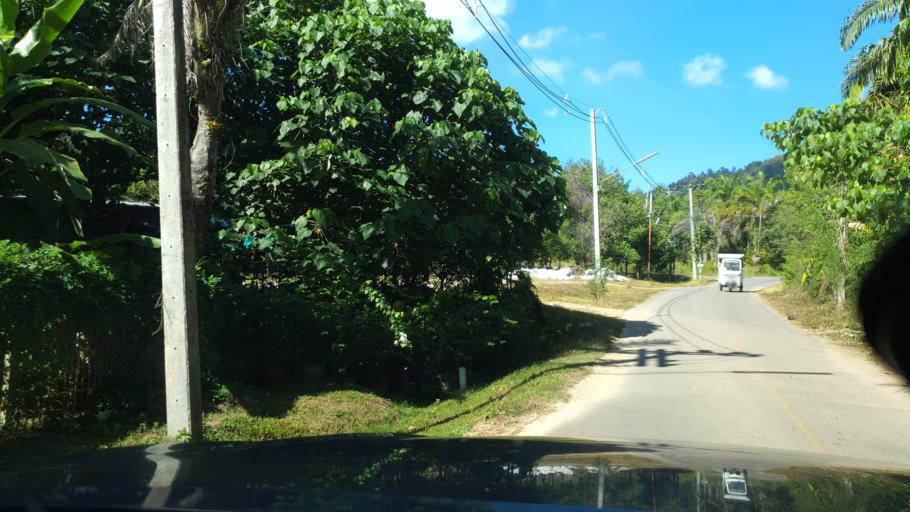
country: TH
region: Phangnga
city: Ban Ao Nang
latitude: 8.0301
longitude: 98.8579
